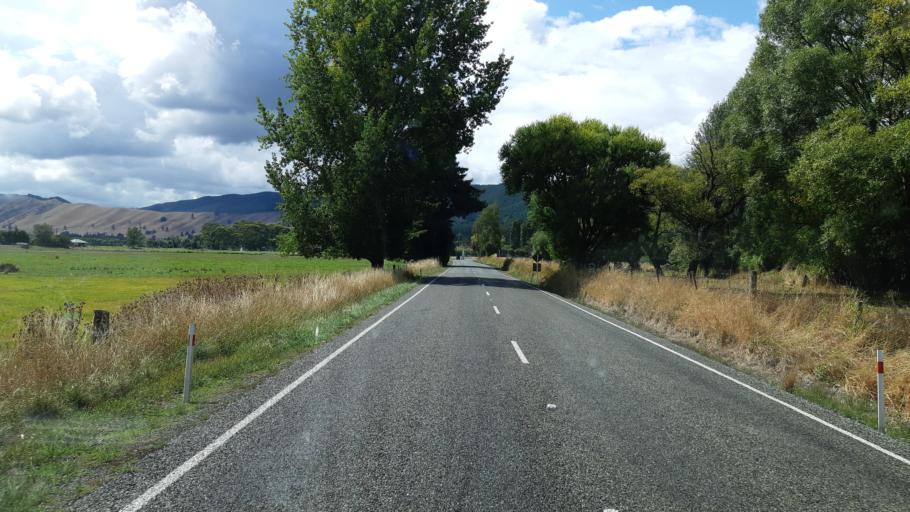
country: NZ
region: Tasman
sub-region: Tasman District
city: Wakefield
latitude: -41.4515
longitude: 172.8233
